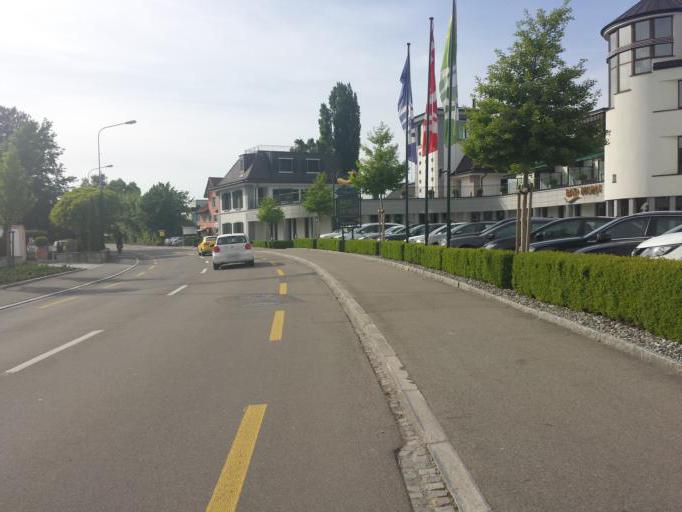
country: CH
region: Saint Gallen
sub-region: Wahlkreis Rorschach
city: Horn
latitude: 47.4944
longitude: 9.4682
